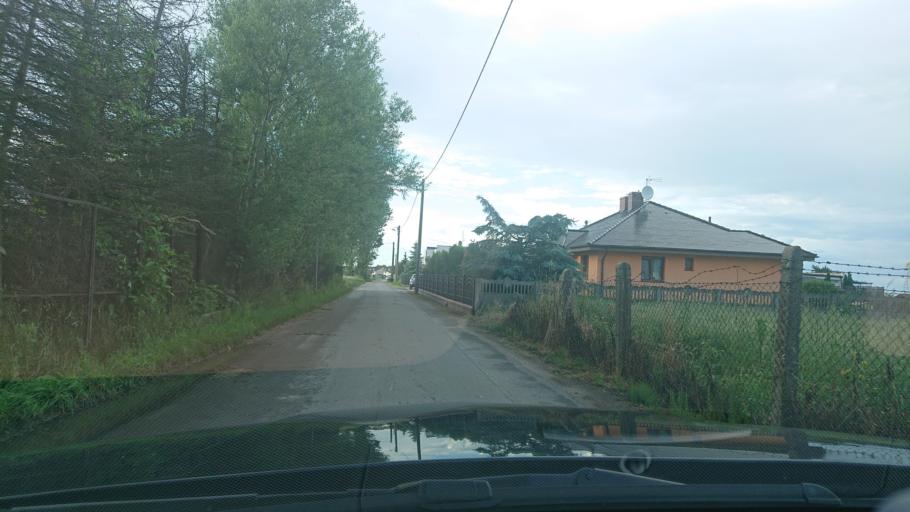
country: PL
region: Greater Poland Voivodeship
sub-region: Powiat gnieznienski
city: Gniezno
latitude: 52.5636
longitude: 17.6145
